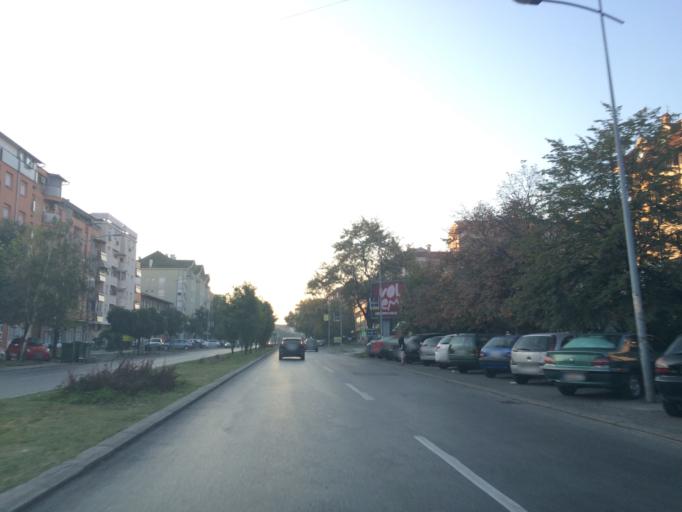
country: RS
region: Autonomna Pokrajina Vojvodina
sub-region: Juznobacki Okrug
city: Novi Sad
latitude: 45.2617
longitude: 19.8197
